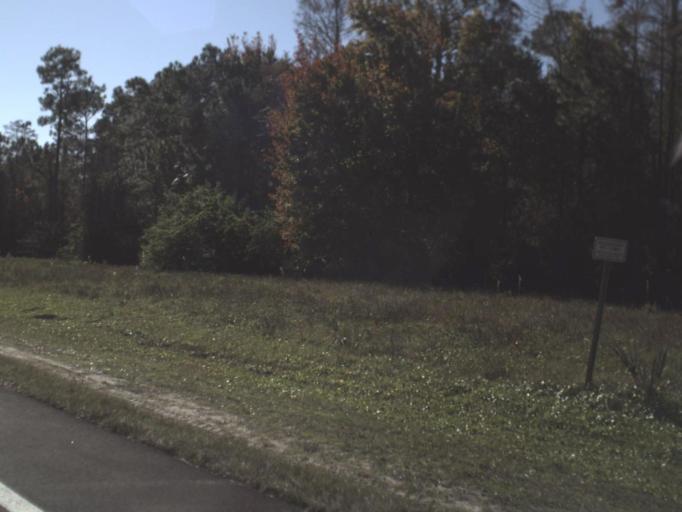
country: US
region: Florida
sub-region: Volusia County
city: South Daytona
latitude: 29.1470
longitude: -81.0606
